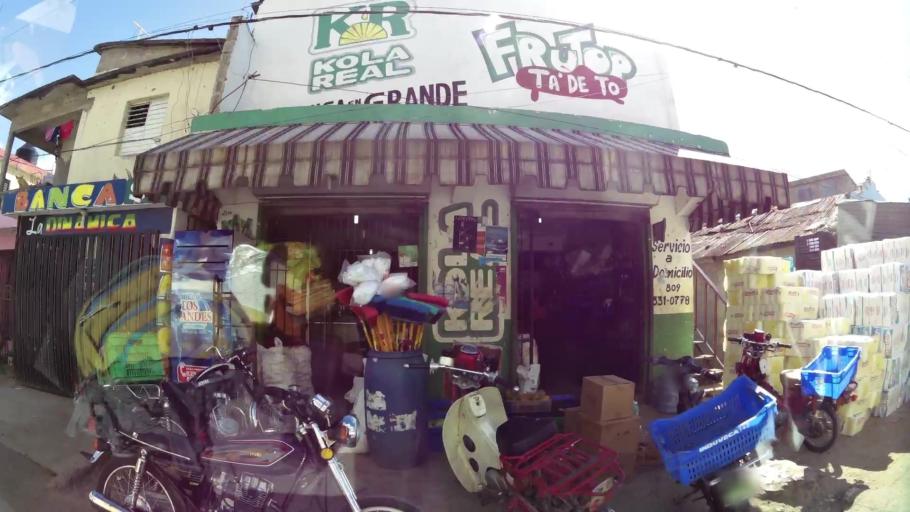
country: DO
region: Santo Domingo
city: Santo Domingo Oeste
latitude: 18.5416
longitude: -70.0410
